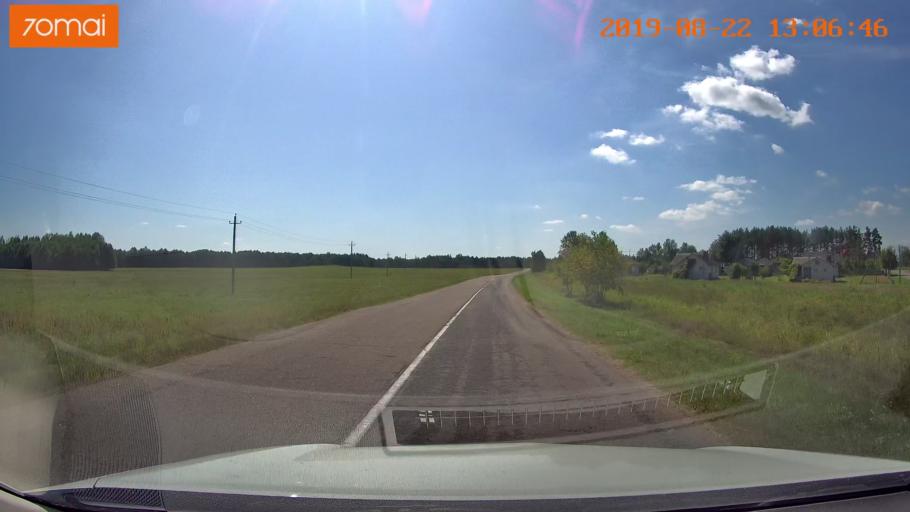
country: BY
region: Minsk
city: Prawdzinski
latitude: 53.3434
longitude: 27.8365
